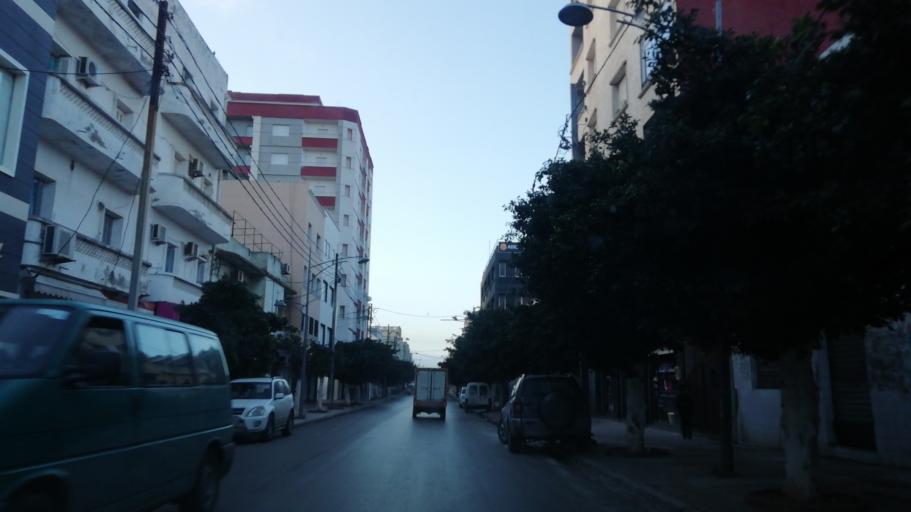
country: DZ
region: Oran
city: Oran
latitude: 35.6829
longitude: -0.6556
